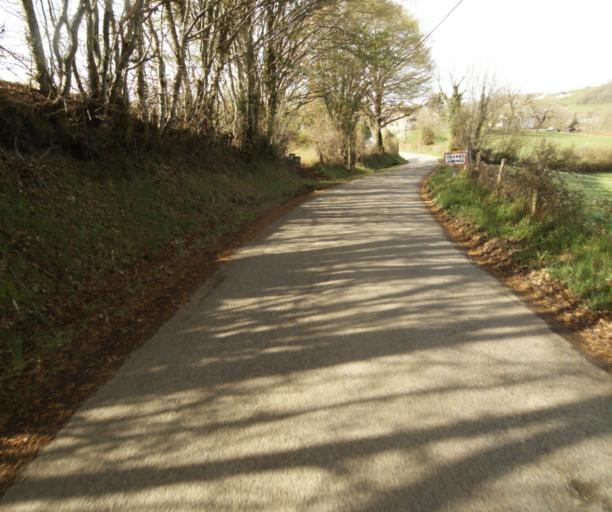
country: FR
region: Limousin
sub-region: Departement de la Correze
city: Laguenne
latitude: 45.2656
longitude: 1.8224
